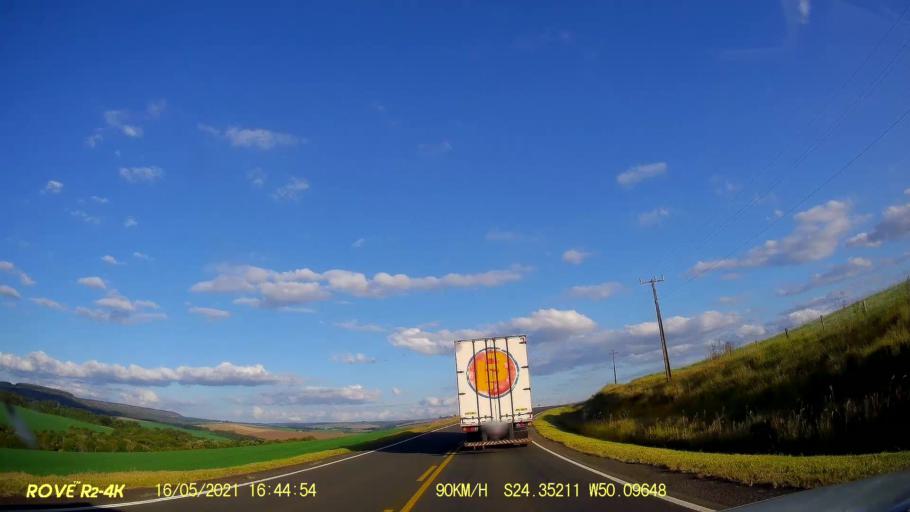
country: BR
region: Parana
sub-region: Pirai Do Sul
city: Pirai do Sul
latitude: -24.3525
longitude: -50.0962
